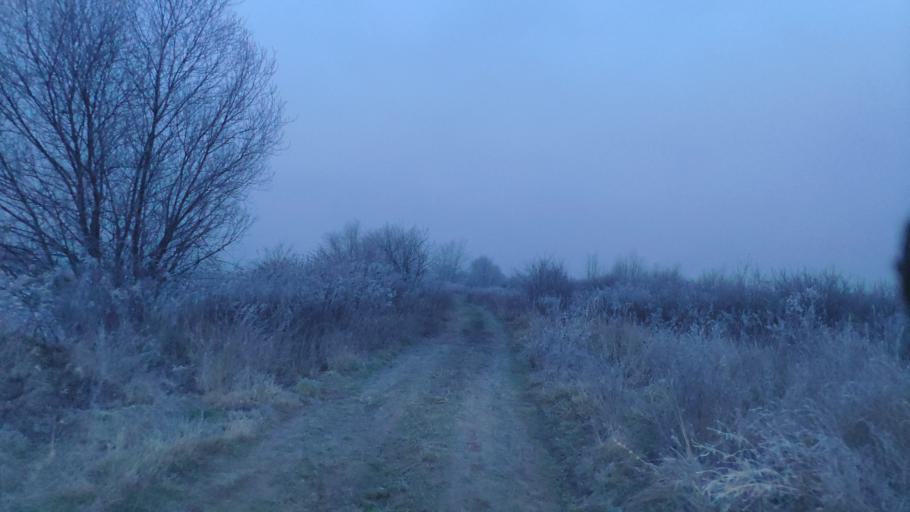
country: SK
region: Kosicky
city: Kosice
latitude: 48.6161
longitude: 21.3352
